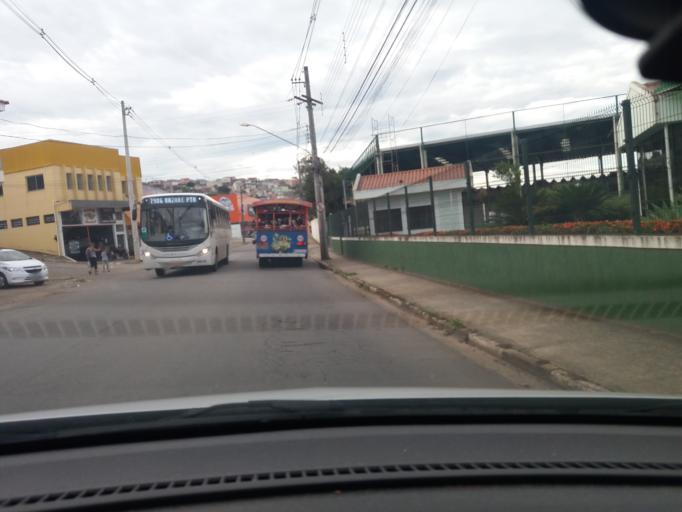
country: BR
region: Sao Paulo
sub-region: Bom Jesus Dos Perdoes
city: Bom Jesus dos Perdoes
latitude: -23.1276
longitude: -46.4690
